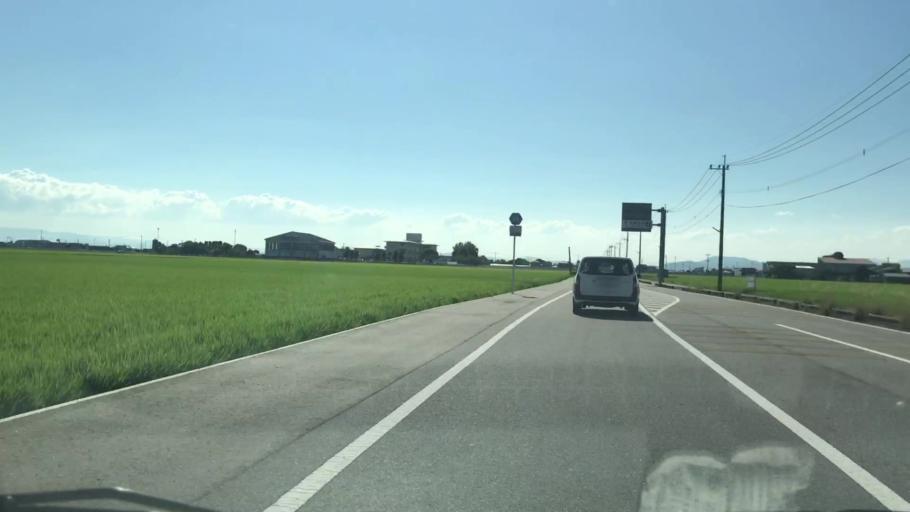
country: JP
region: Saga Prefecture
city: Okawa
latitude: 33.2205
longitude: 130.3507
